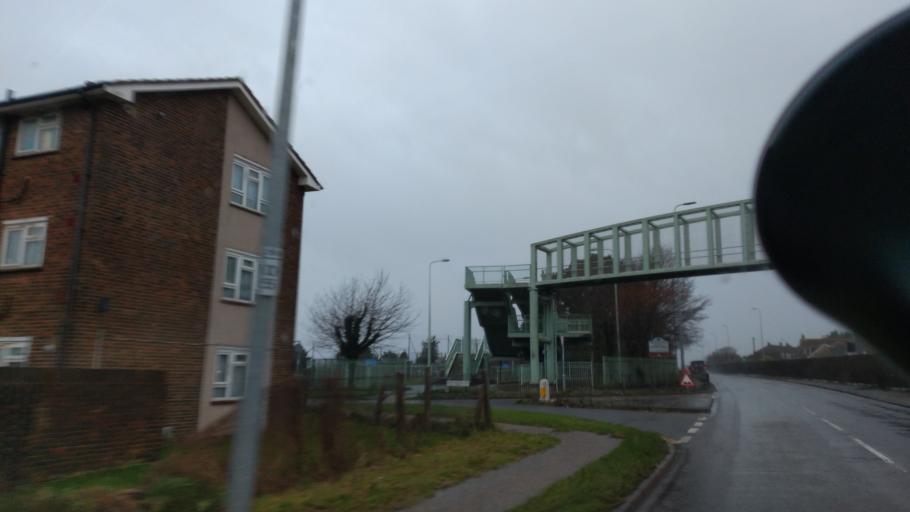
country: GB
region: England
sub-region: West Sussex
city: Lancing
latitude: 50.8371
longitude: -0.3288
